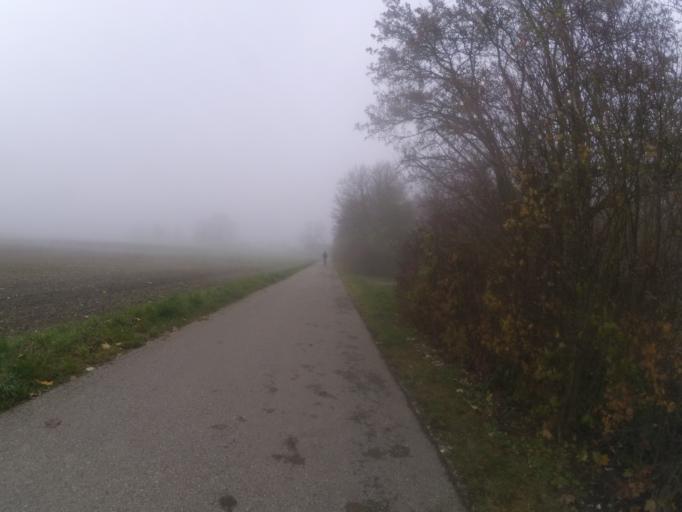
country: DE
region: Bavaria
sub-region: Swabia
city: Neu-Ulm
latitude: 48.3726
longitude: 10.0141
